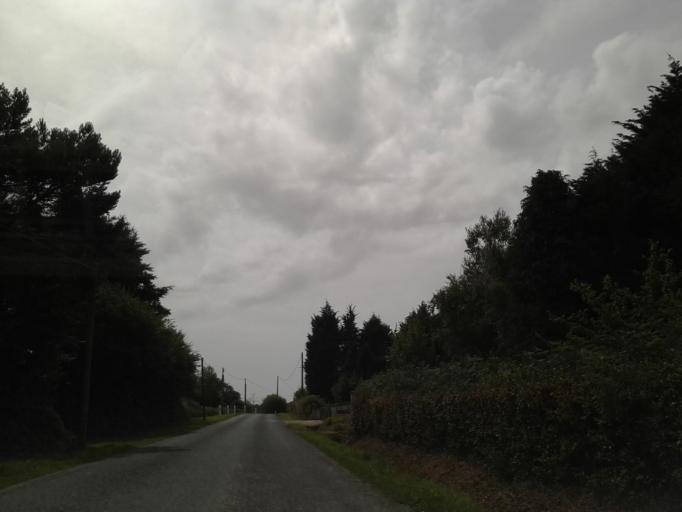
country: FR
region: Lower Normandy
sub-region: Departement de la Manche
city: Bricquebec
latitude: 49.4695
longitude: -1.7156
